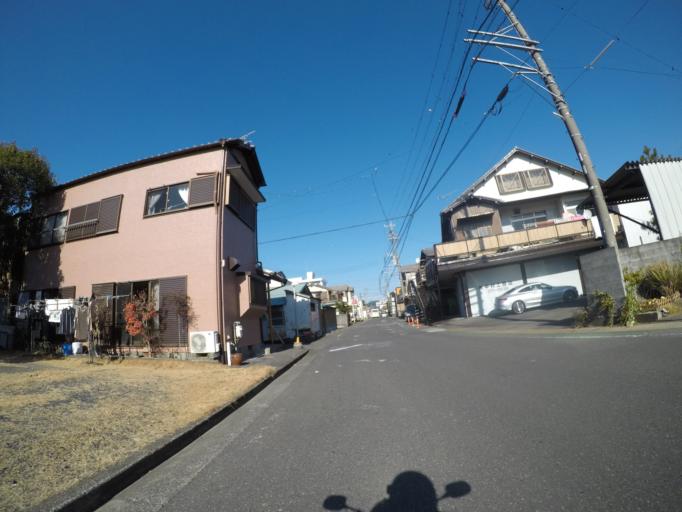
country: JP
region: Shizuoka
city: Shizuoka-shi
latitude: 34.9935
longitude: 138.3610
